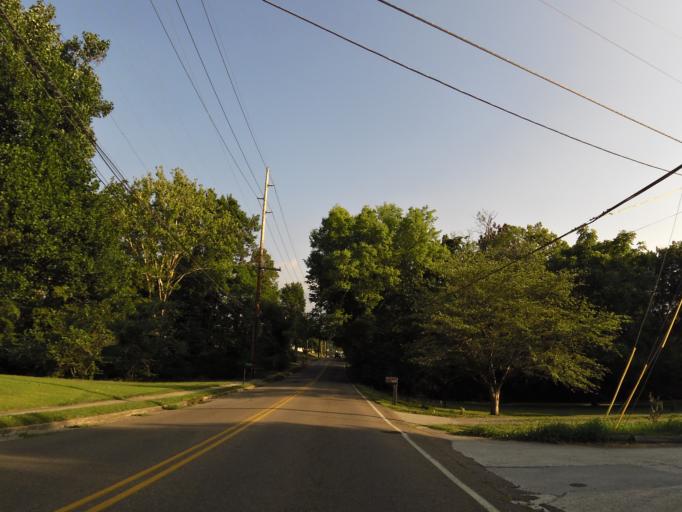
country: US
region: Tennessee
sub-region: Knox County
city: Knoxville
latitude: 36.0313
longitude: -83.9222
